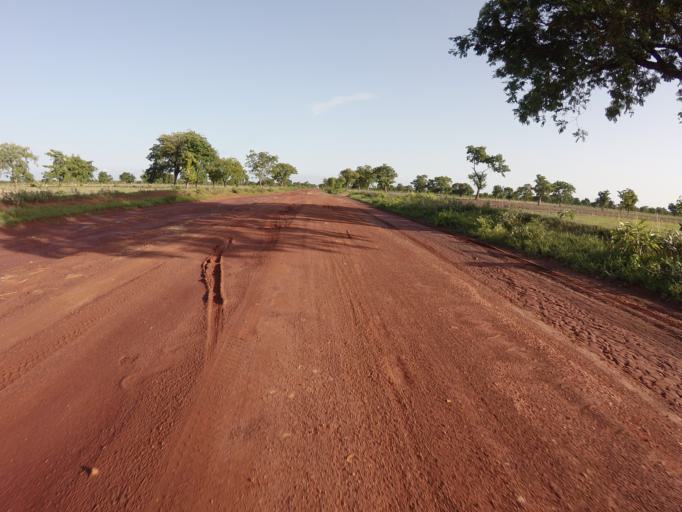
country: TG
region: Savanes
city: Sansanne-Mango
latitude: 10.3727
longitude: -0.0942
